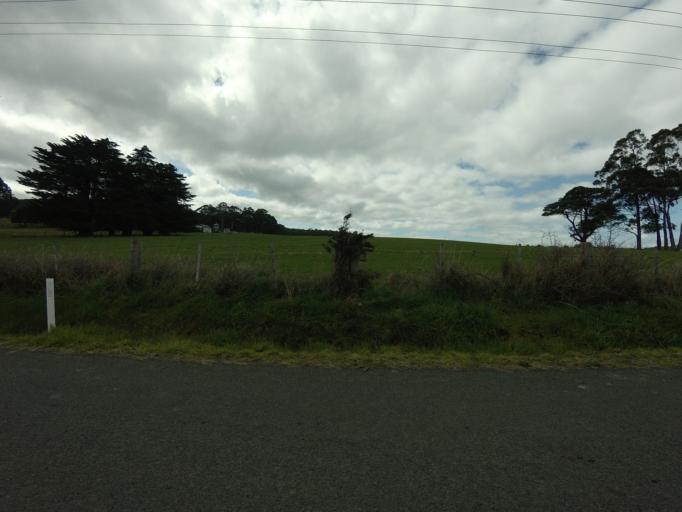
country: AU
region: Tasmania
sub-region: Huon Valley
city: Geeveston
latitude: -43.4332
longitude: 146.9785
